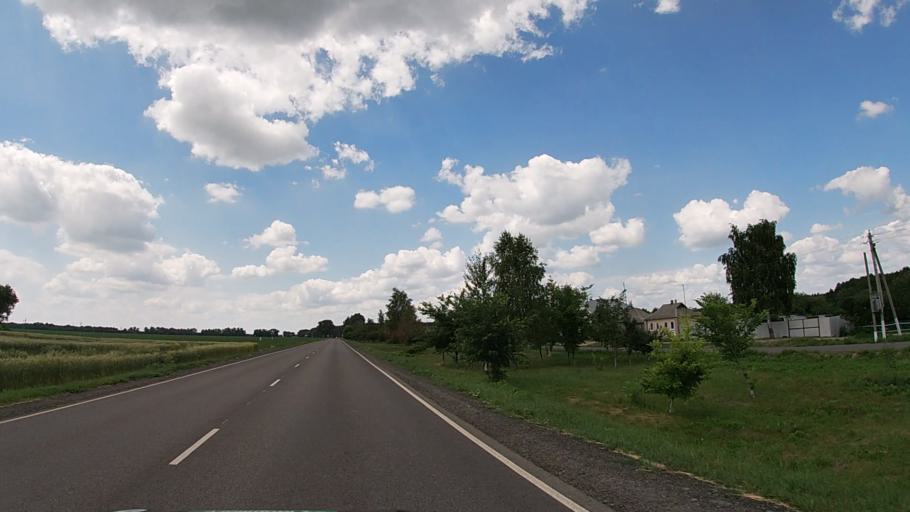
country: RU
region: Belgorod
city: Golovchino
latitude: 50.5107
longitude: 35.7571
